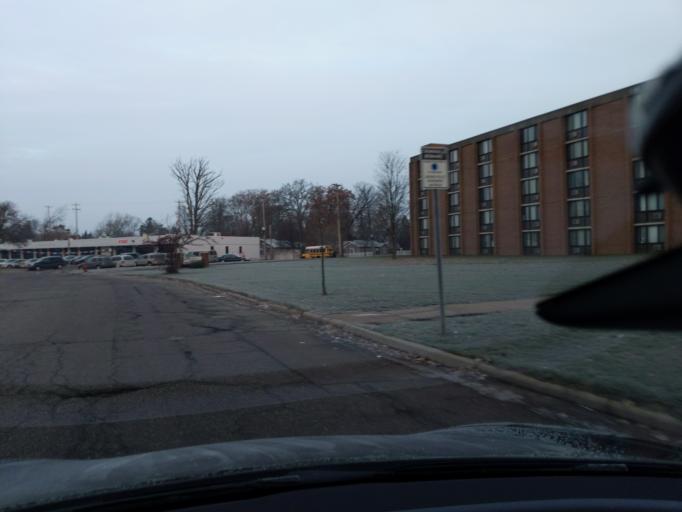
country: US
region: Michigan
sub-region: Ingham County
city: Lansing
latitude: 42.6997
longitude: -84.5629
